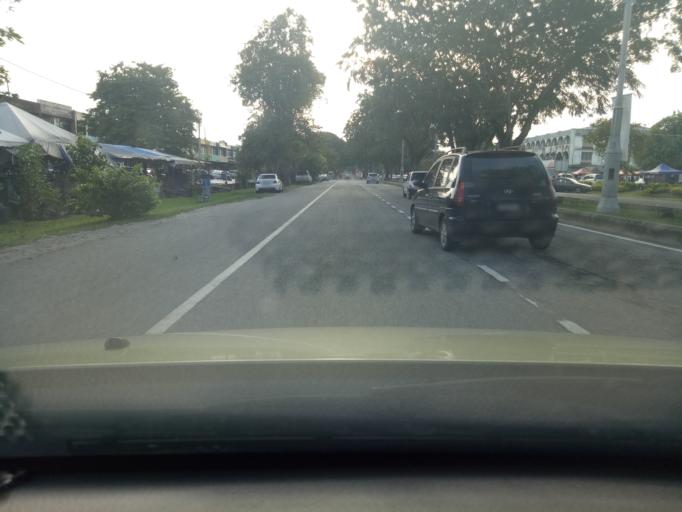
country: MY
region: Kedah
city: Alor Setar
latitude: 6.1428
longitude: 100.3600
